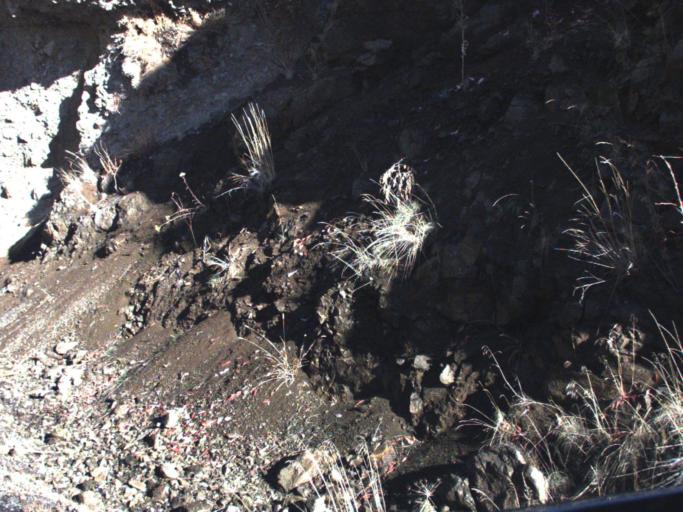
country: US
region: Washington
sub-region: Asotin County
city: Asotin
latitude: 46.0558
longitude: -117.2378
